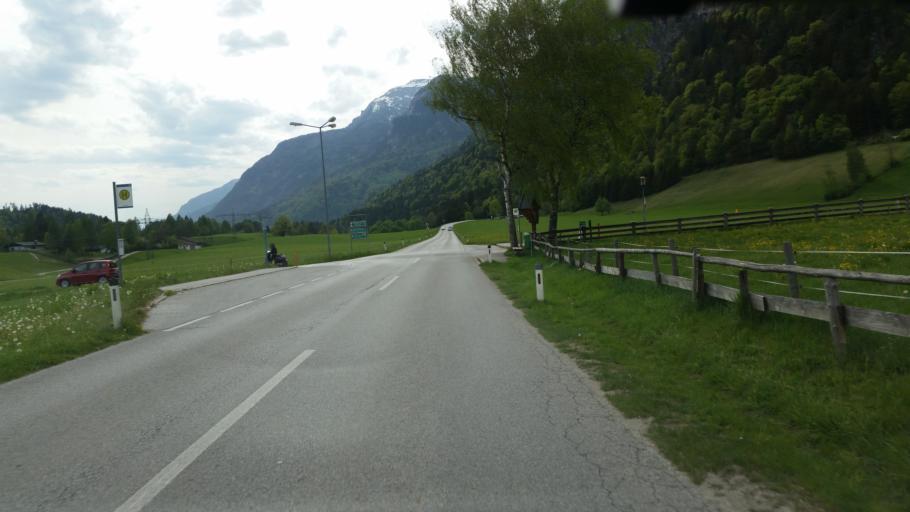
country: AT
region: Tyrol
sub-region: Politischer Bezirk Kufstein
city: Radfeld
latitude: 47.4653
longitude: 11.9071
